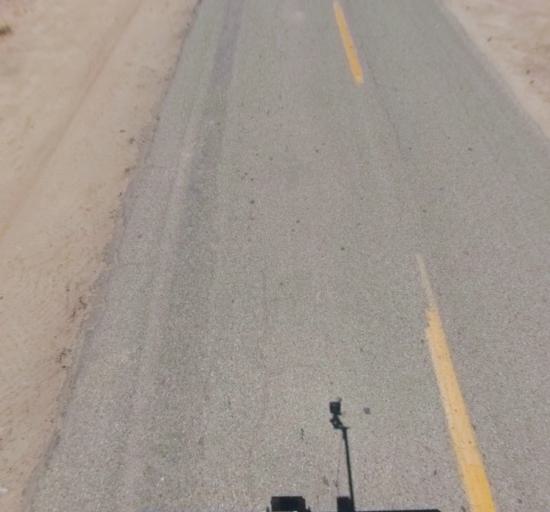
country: US
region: California
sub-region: Madera County
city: Chowchilla
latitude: 37.0907
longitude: -120.2755
